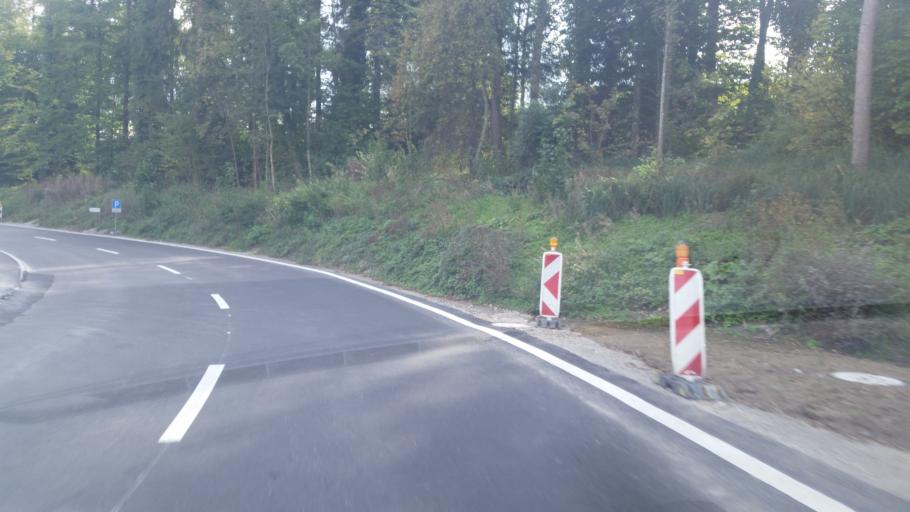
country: CH
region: Aargau
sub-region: Bezirk Baden
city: Kunten
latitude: 47.3935
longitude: 8.3016
